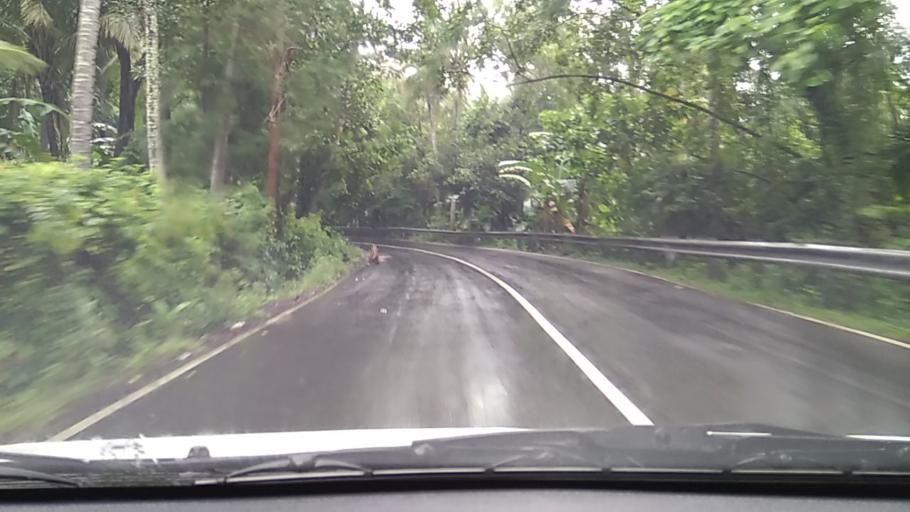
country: ID
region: Bali
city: Banjar Bugbug
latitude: -8.5001
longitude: 115.5832
